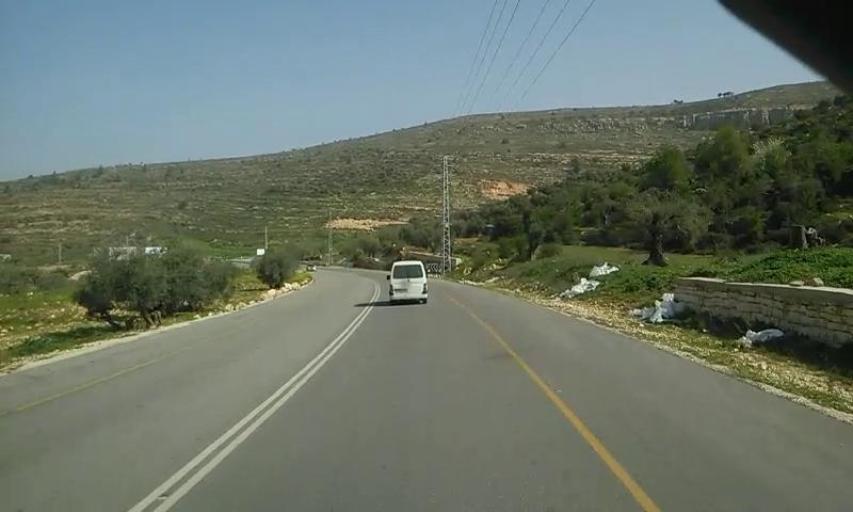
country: PS
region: West Bank
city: Dura al Qar`
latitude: 31.9792
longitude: 35.2351
